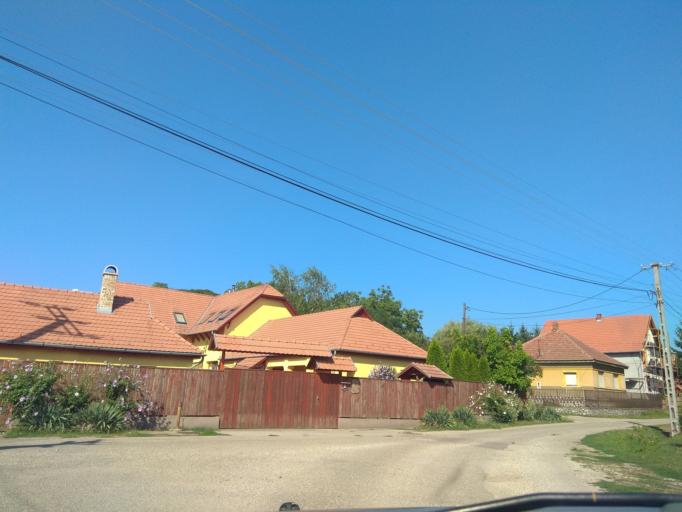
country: HU
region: Borsod-Abauj-Zemplen
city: Harsany
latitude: 47.9816
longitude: 20.7850
